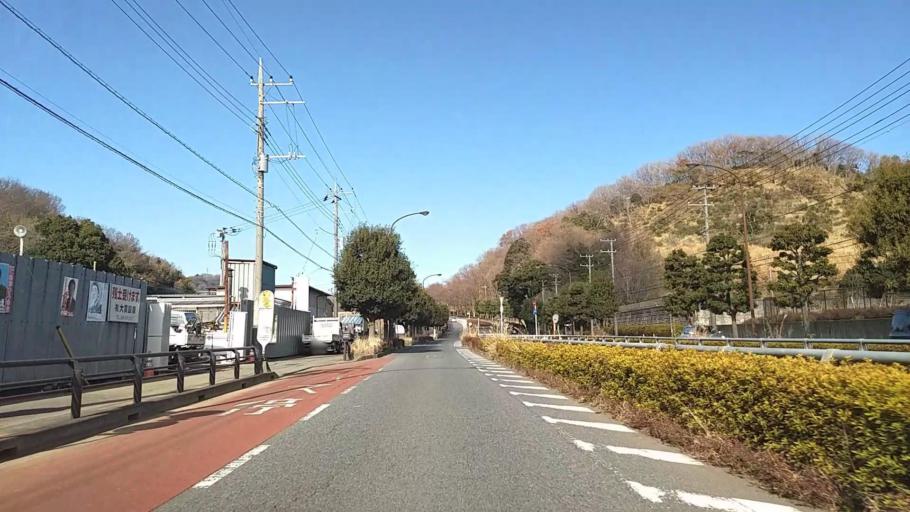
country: JP
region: Kanagawa
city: Atsugi
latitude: 35.4366
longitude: 139.3135
